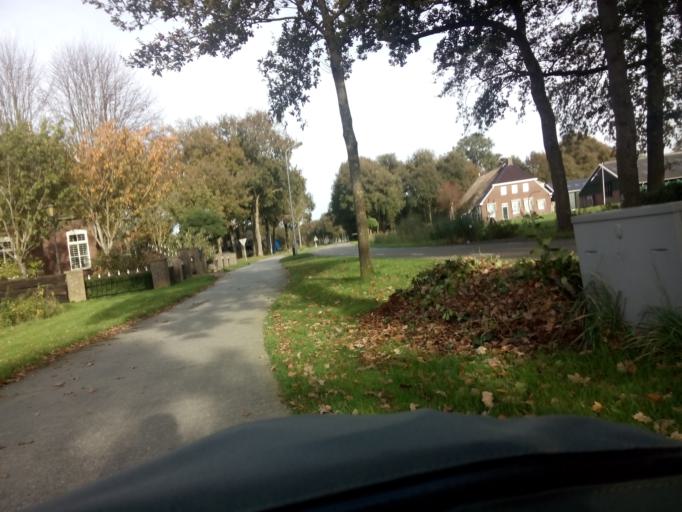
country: NL
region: Drenthe
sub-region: Gemeente Hoogeveen
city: Hoogeveen
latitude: 52.7876
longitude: 6.4508
